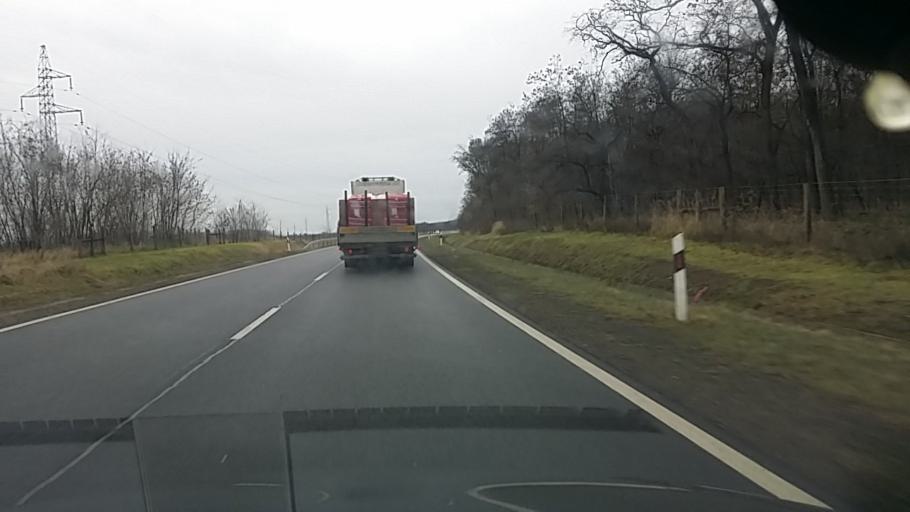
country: HU
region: Hajdu-Bihar
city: Hajduhadhaz
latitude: 47.6334
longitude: 21.6465
